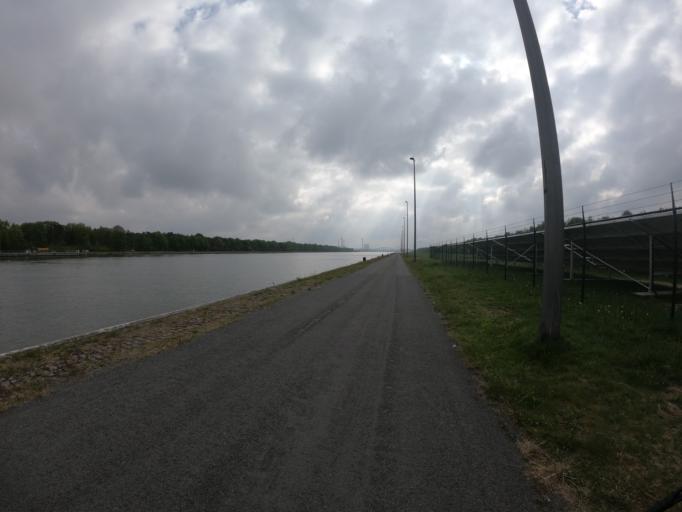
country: BE
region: Flanders
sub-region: Provincie Limburg
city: Diepenbeek
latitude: 50.9371
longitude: 5.4381
